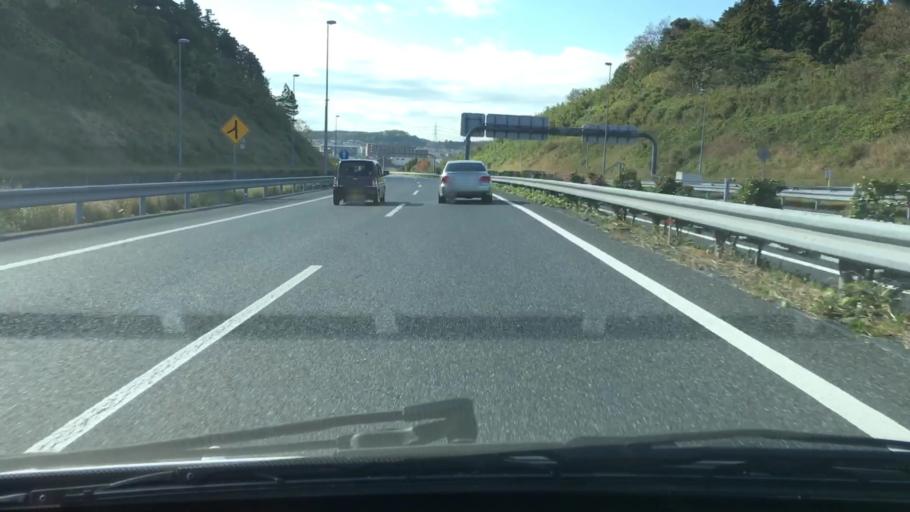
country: JP
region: Chiba
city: Kisarazu
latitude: 35.3532
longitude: 139.9477
